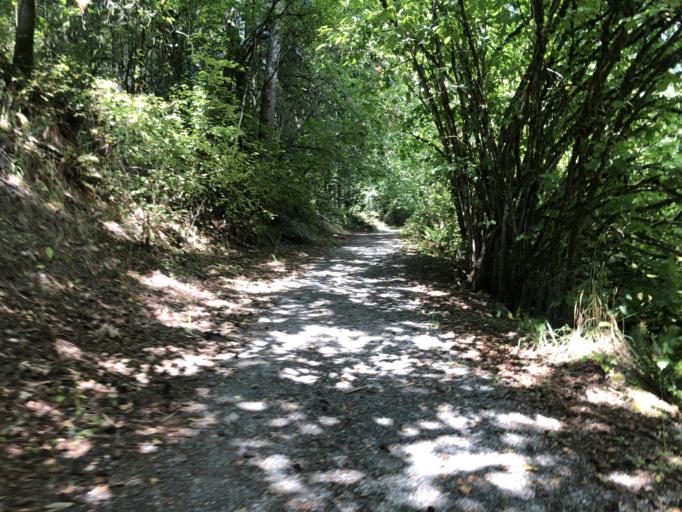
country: US
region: Washington
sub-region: King County
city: Lea Hill
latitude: 47.3438
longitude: -122.2050
